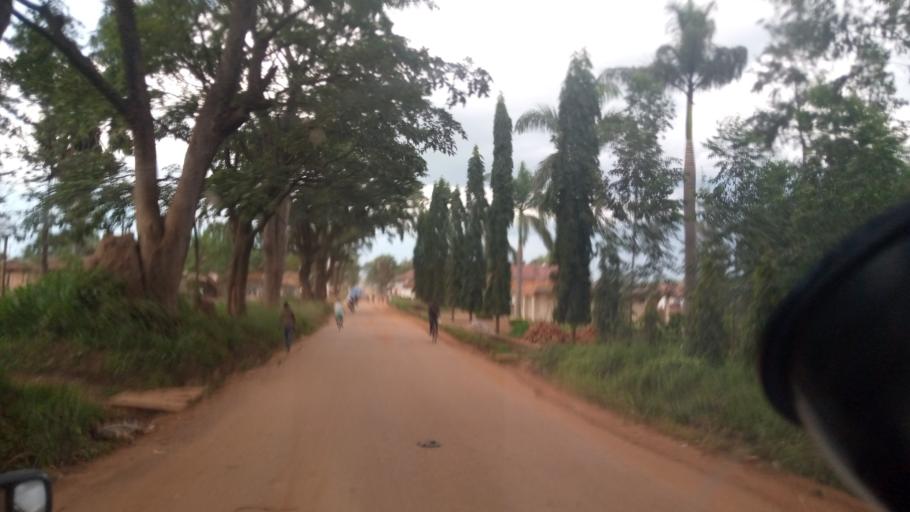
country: UG
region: Northern Region
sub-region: Lira District
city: Lira
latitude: 2.2534
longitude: 32.9039
